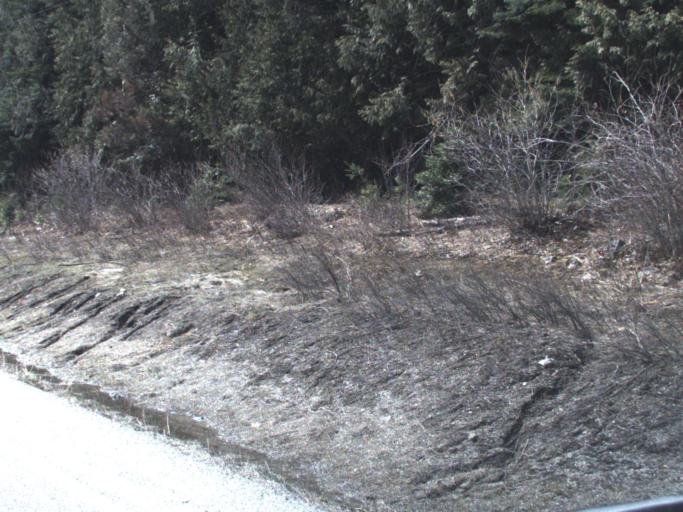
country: US
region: Washington
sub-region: Pend Oreille County
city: Newport
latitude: 48.4555
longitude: -117.3267
